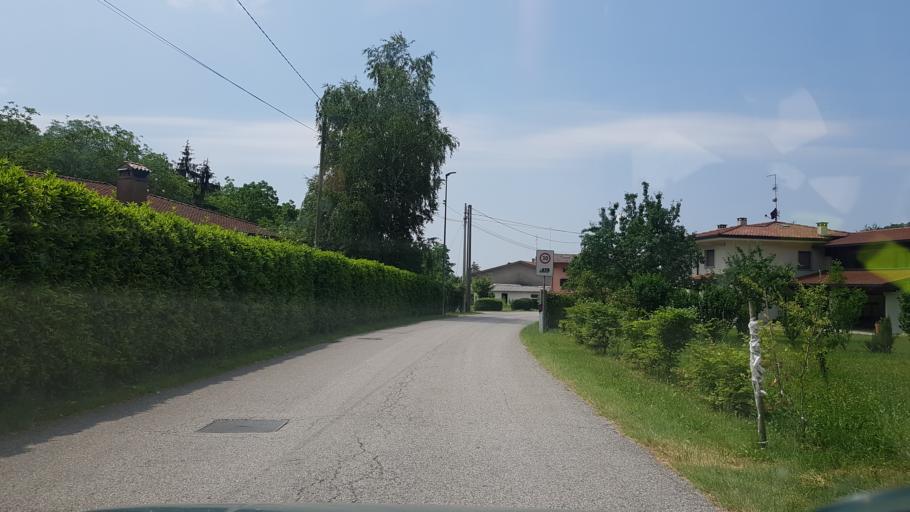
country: IT
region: Friuli Venezia Giulia
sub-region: Provincia di Udine
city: Torreano
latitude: 46.1348
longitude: 13.4380
